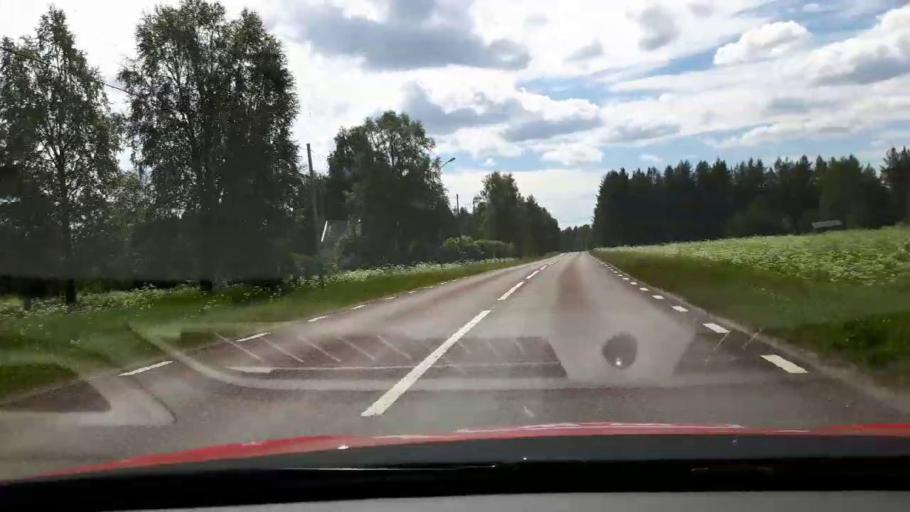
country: SE
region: Jaemtland
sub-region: Harjedalens Kommun
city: Sveg
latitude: 62.1550
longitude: 14.9539
